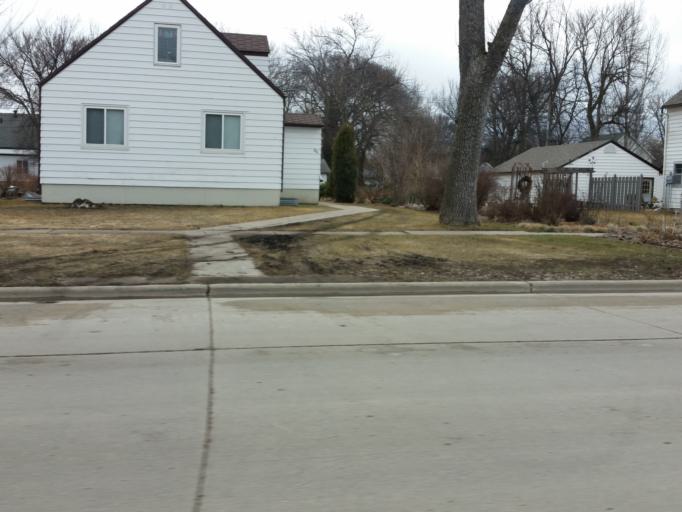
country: US
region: North Dakota
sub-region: Cass County
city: Casselton
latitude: 46.9047
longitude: -97.2109
